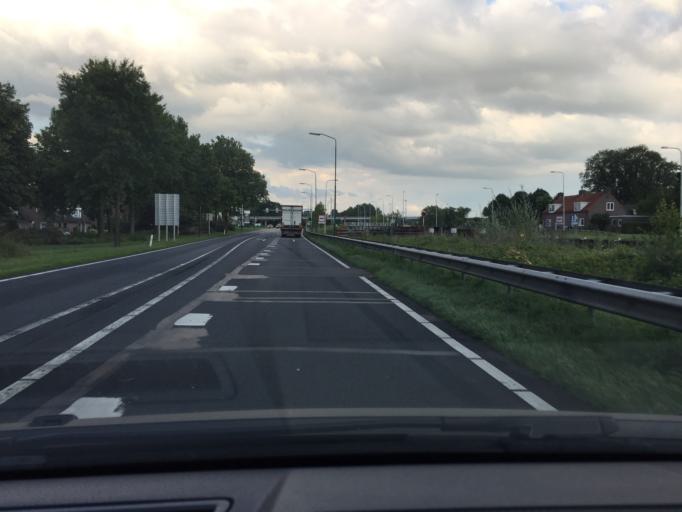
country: NL
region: North Brabant
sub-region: Gemeente Veghel
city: Veghel
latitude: 51.6103
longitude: 5.5289
